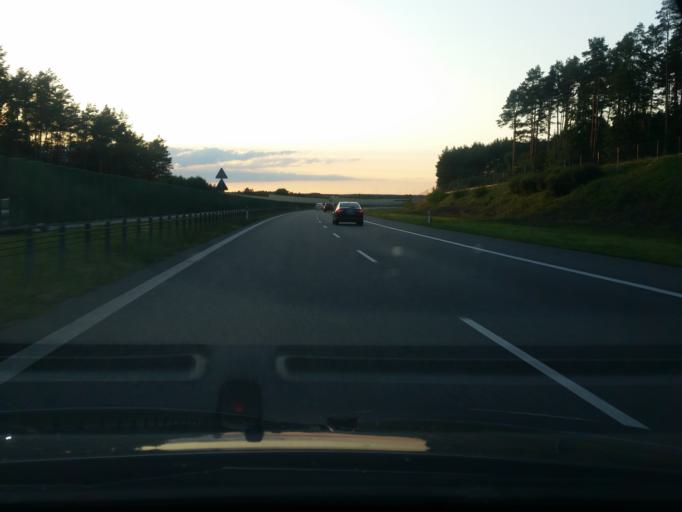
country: PL
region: Kujawsko-Pomorskie
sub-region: Powiat swiecki
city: Warlubie
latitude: 53.4600
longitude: 18.6262
